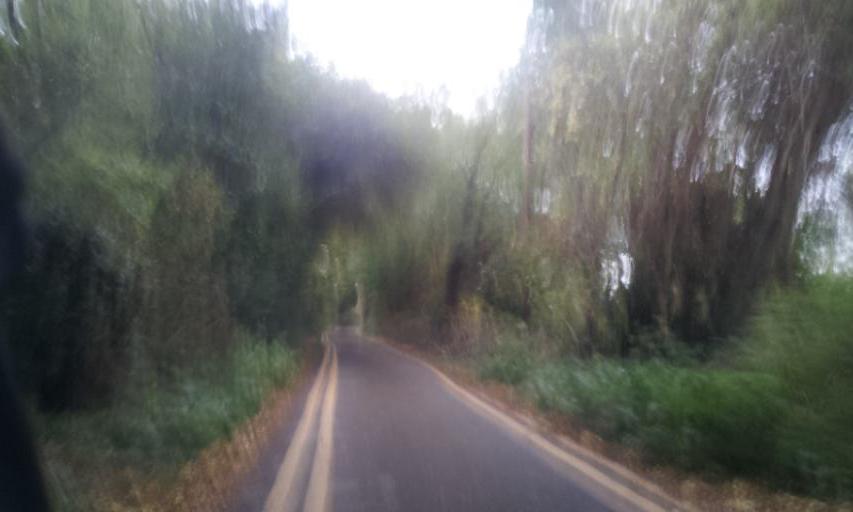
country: GB
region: England
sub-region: Kent
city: Snodland
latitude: 51.3141
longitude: 0.4348
